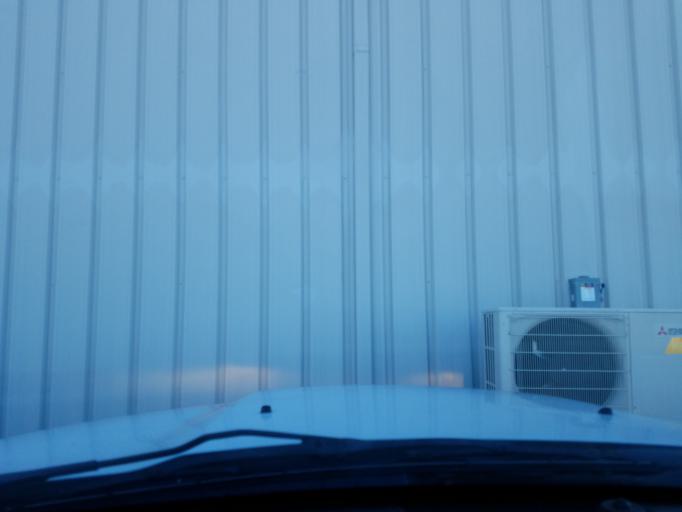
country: US
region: Indiana
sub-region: Dubois County
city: Ferdinand
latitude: 38.2165
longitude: -86.8662
